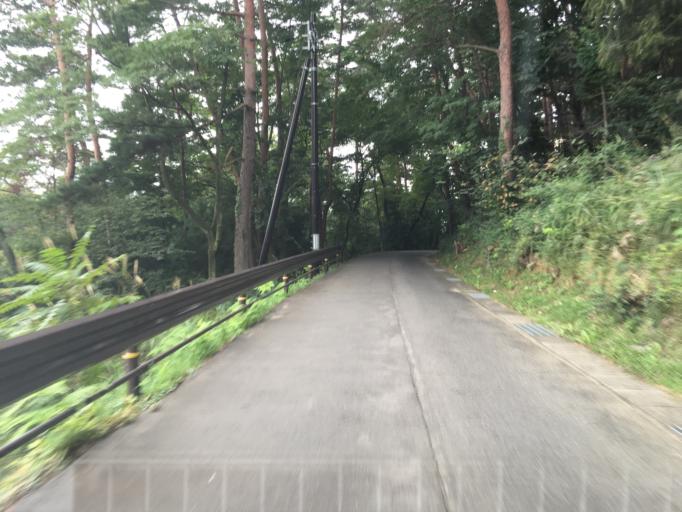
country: JP
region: Fukushima
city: Fukushima-shi
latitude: 37.7741
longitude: 140.4807
